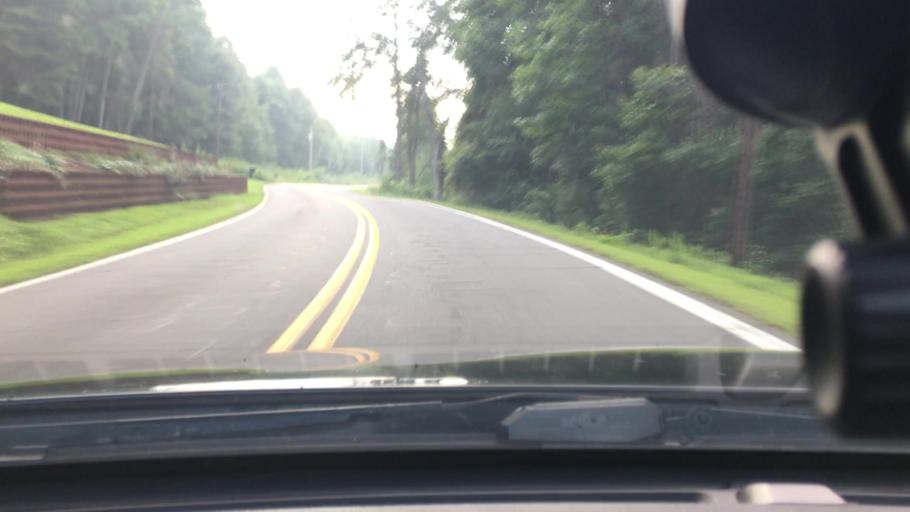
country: US
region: North Carolina
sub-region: Rutherford County
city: Rutherfordton
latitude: 35.3764
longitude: -81.9758
